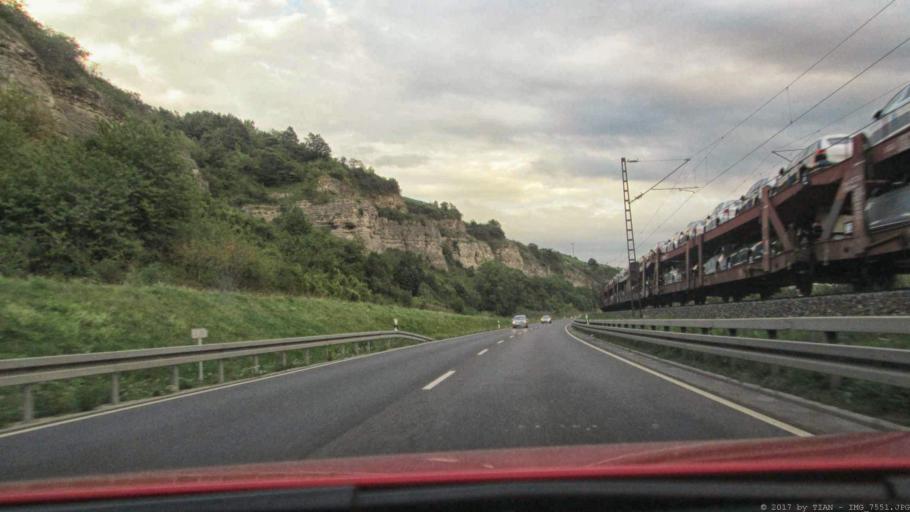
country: DE
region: Bavaria
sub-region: Regierungsbezirk Unterfranken
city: Himmelstadt
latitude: 49.9399
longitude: 9.8039
